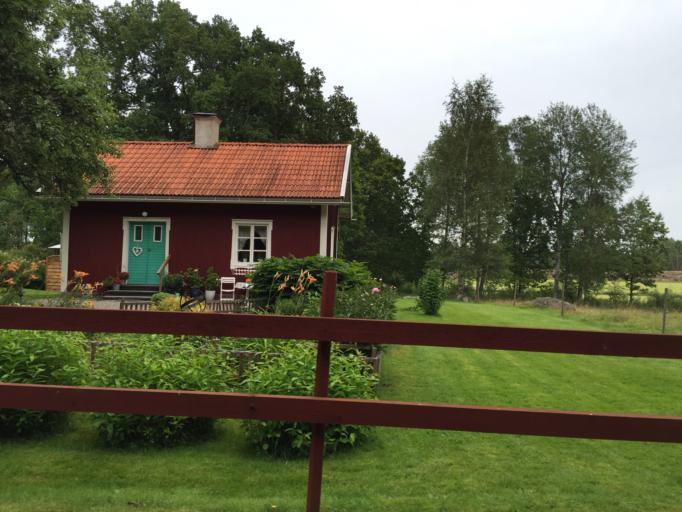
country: SE
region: Soedermanland
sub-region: Vingakers Kommun
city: Vingaker
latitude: 59.0098
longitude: 15.7997
